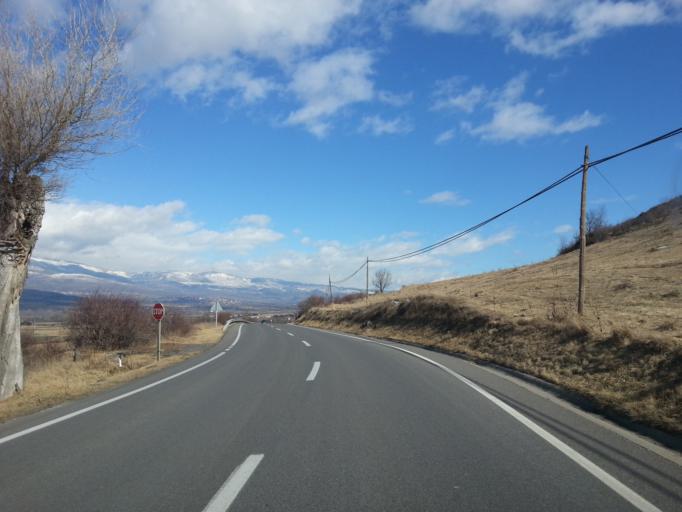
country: ES
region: Catalonia
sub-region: Provincia de Girona
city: Das
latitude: 42.3654
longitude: 1.8759
